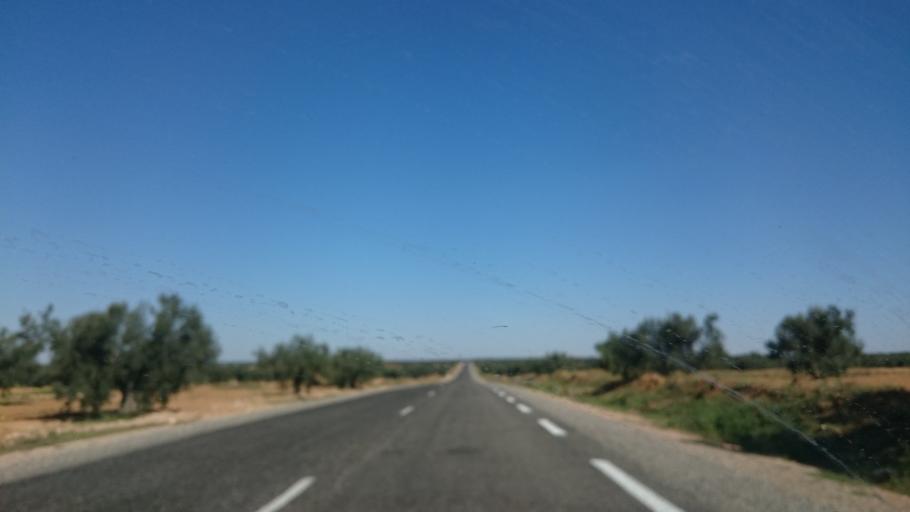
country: TN
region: Safaqis
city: Sfax
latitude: 34.8224
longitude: 10.4711
